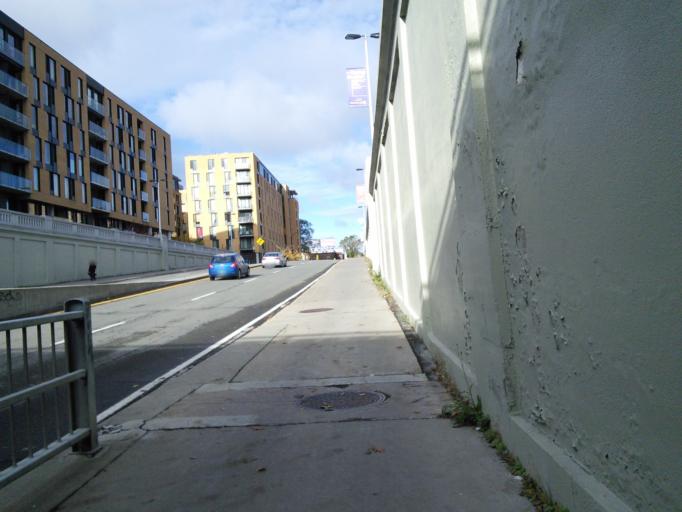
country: CA
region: Quebec
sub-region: Montreal
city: Montreal
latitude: 45.5320
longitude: -73.5946
